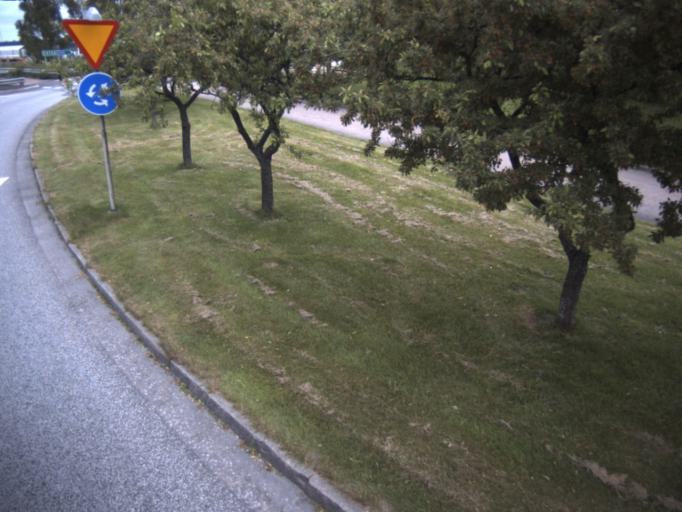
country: SE
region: Skane
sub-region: Helsingborg
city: Odakra
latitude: 56.0674
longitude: 12.7221
